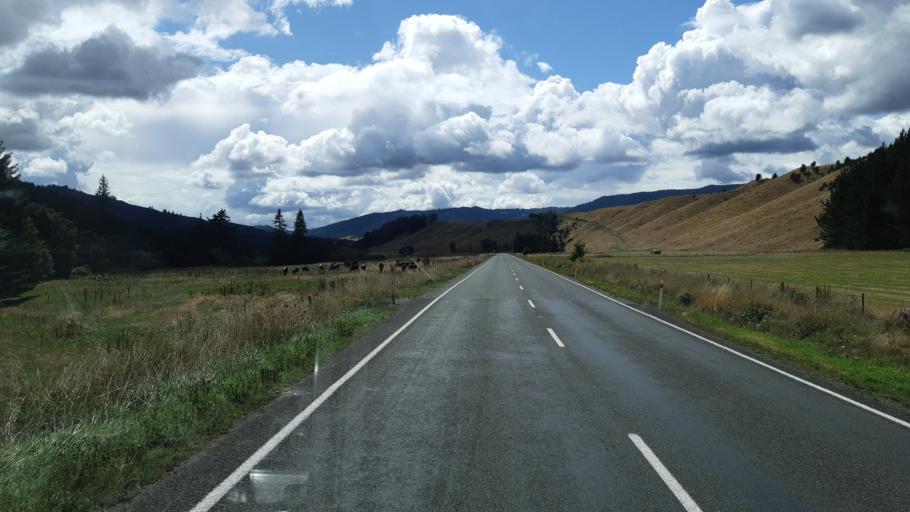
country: NZ
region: Tasman
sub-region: Tasman District
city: Wakefield
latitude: -41.5757
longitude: 172.7705
